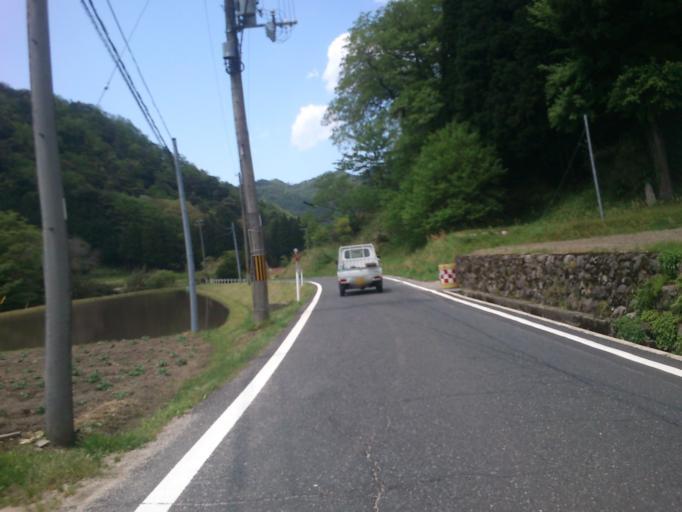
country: JP
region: Kyoto
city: Miyazu
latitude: 35.6861
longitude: 135.1517
